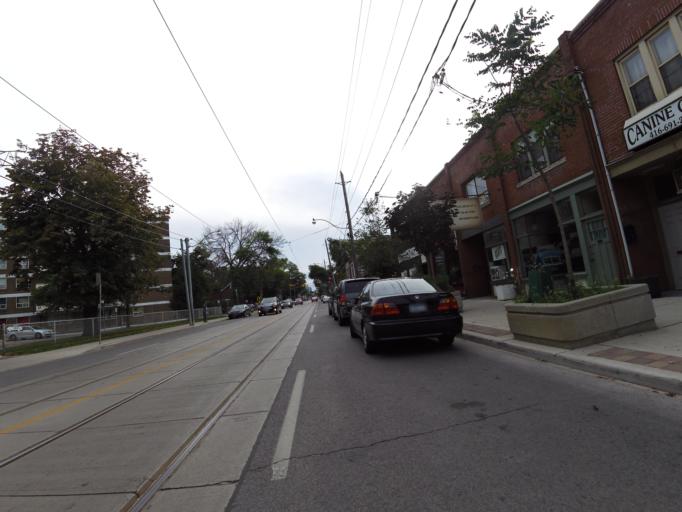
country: CA
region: Ontario
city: Toronto
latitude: 43.6660
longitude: -79.3181
